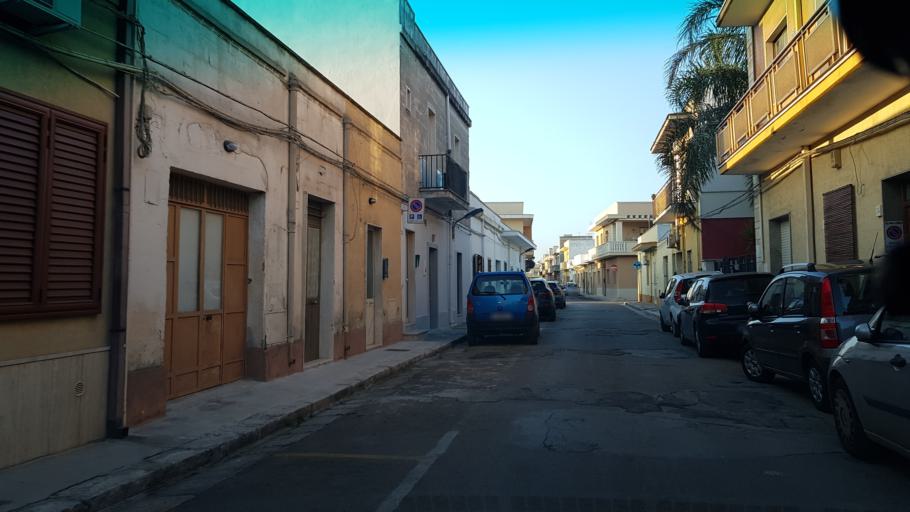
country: IT
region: Apulia
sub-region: Provincia di Brindisi
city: Mesagne
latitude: 40.5532
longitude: 17.8037
